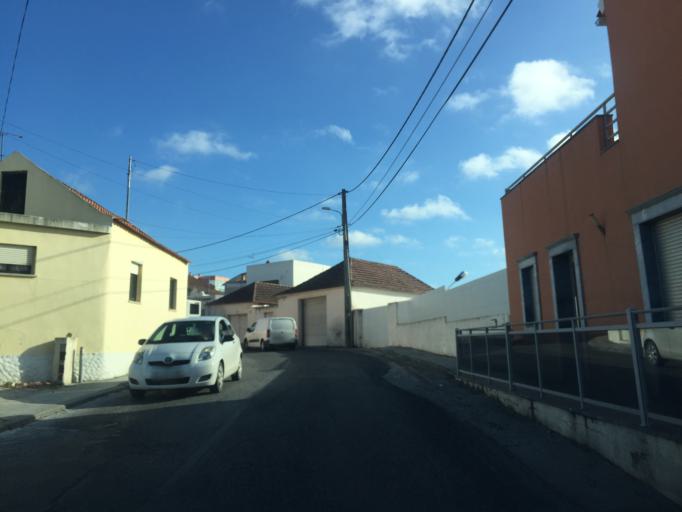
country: PT
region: Lisbon
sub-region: Torres Vedras
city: A dos Cunhados
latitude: 39.1538
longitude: -9.2983
